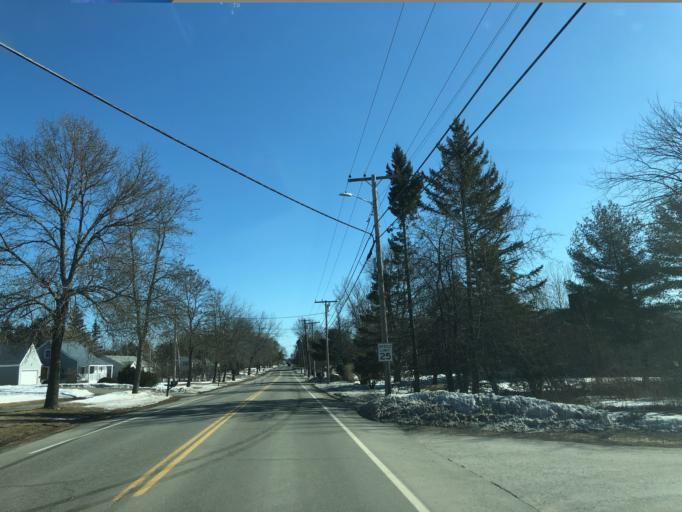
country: US
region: Maine
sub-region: Penobscot County
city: Brewer
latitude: 44.8172
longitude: -68.7520
